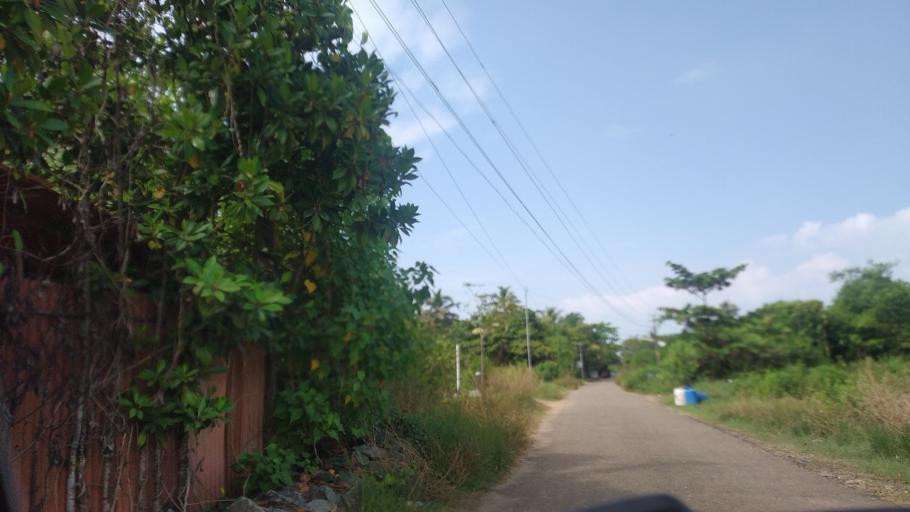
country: IN
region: Kerala
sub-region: Ernakulam
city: Elur
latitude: 10.0539
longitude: 76.2026
